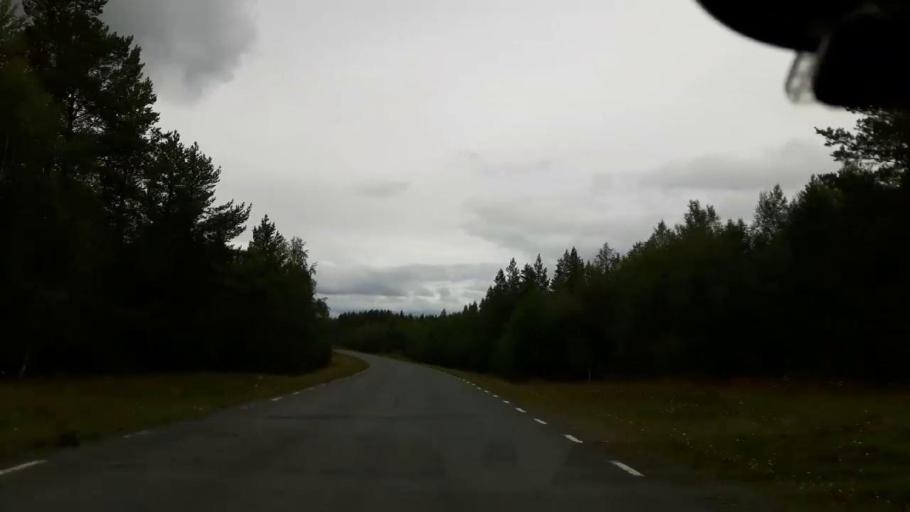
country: SE
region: Jaemtland
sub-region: Krokoms Kommun
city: Valla
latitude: 63.6271
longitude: 13.8158
